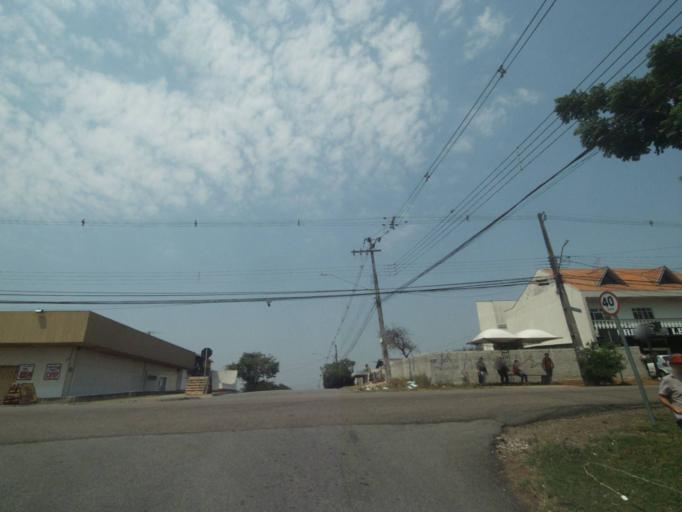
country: BR
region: Parana
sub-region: Sao Jose Dos Pinhais
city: Sao Jose dos Pinhais
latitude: -25.5360
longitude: -49.2463
